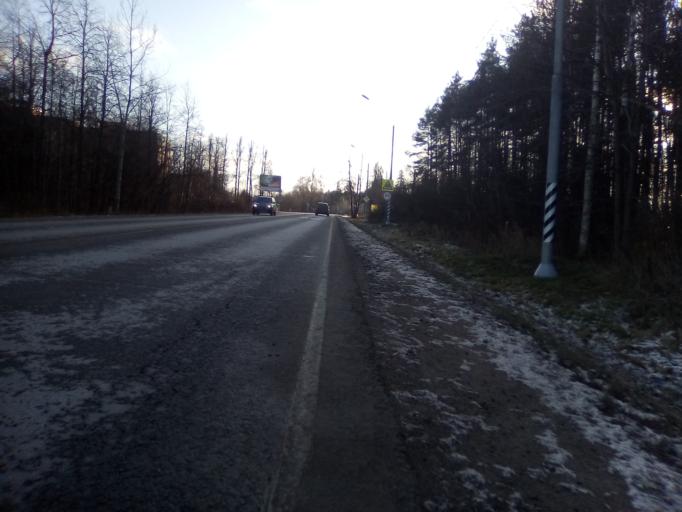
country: RU
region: Moskovskaya
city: Lesnoy Gorodok
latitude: 55.6706
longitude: 37.1724
